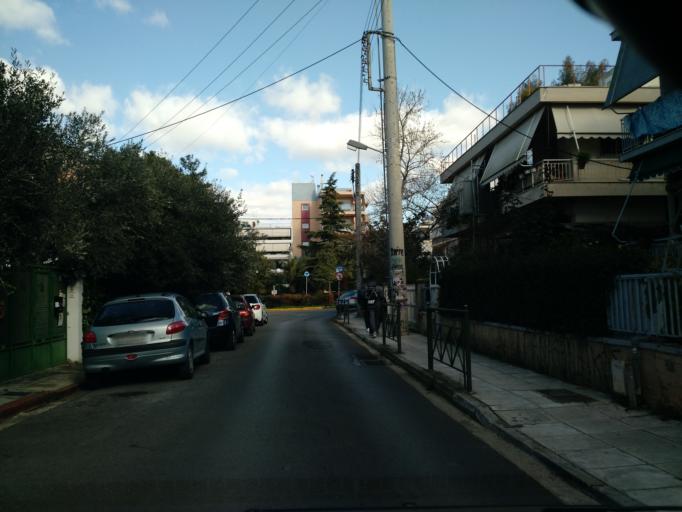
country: GR
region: Attica
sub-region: Nomarchia Athinas
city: Agia Paraskevi
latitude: 38.0105
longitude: 23.8328
